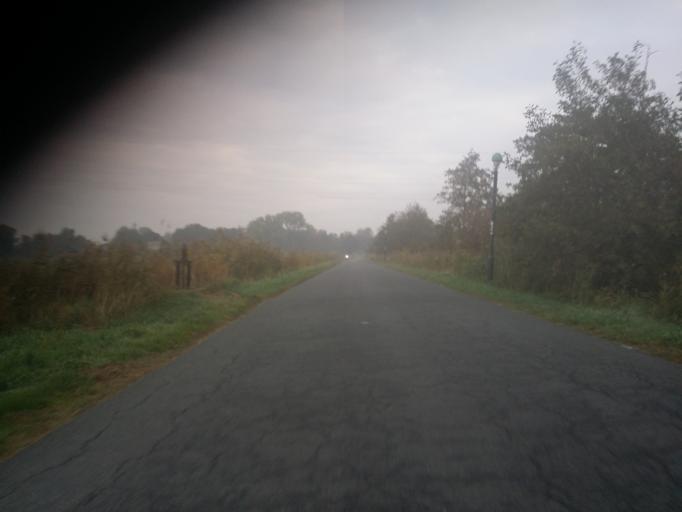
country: DE
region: Lower Saxony
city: Lilienthal
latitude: 53.1265
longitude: 8.8608
